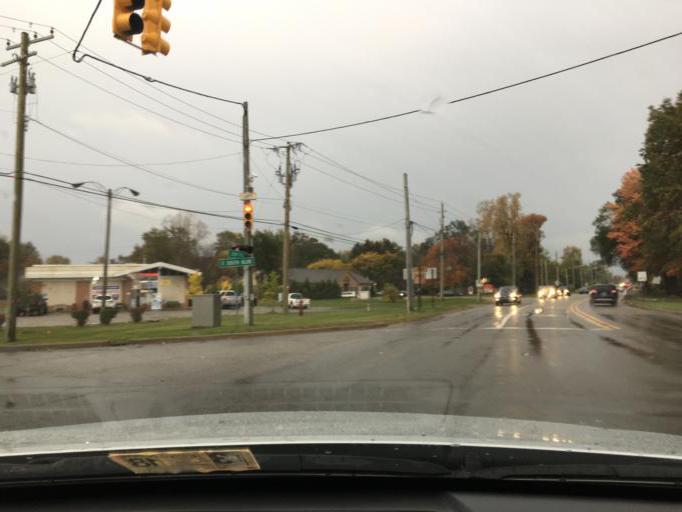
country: US
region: Michigan
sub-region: Oakland County
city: Troy
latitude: 42.6236
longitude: -83.1108
